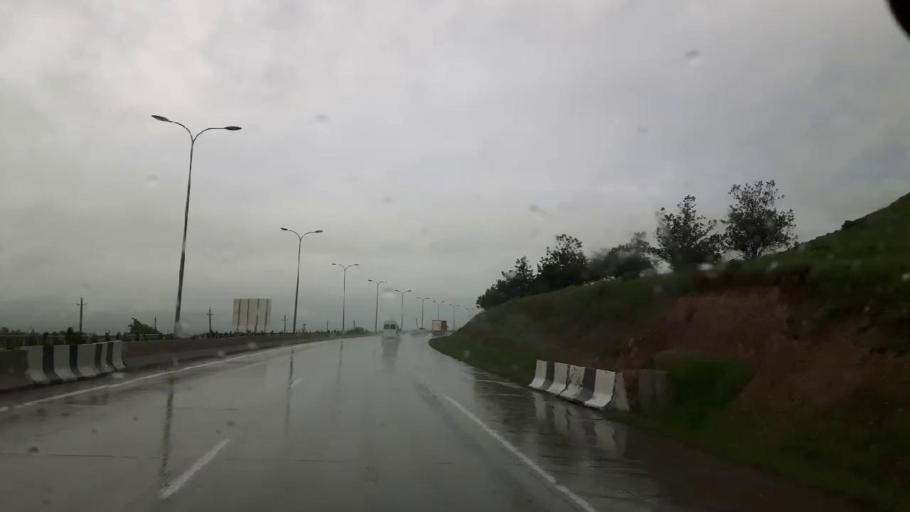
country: GE
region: Shida Kartli
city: Gori
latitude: 42.0265
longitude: 44.1839
